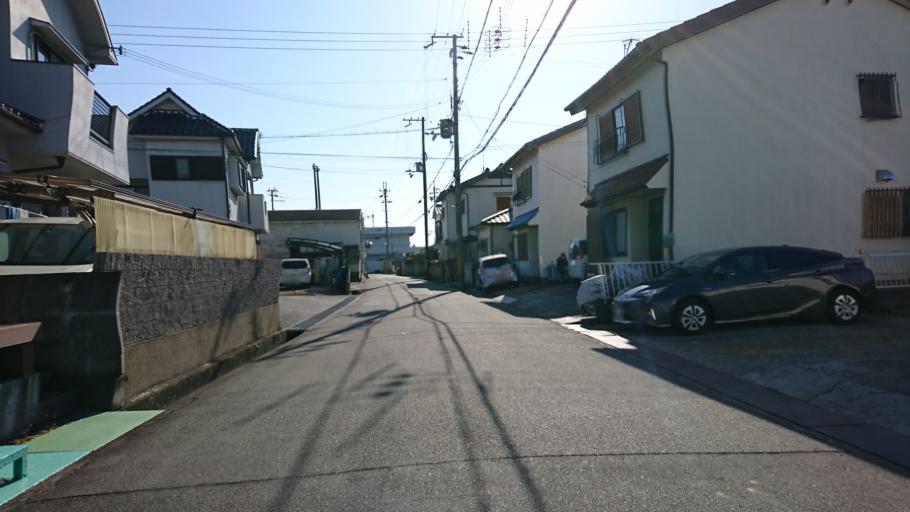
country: JP
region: Hyogo
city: Kakogawacho-honmachi
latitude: 34.7427
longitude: 134.8441
